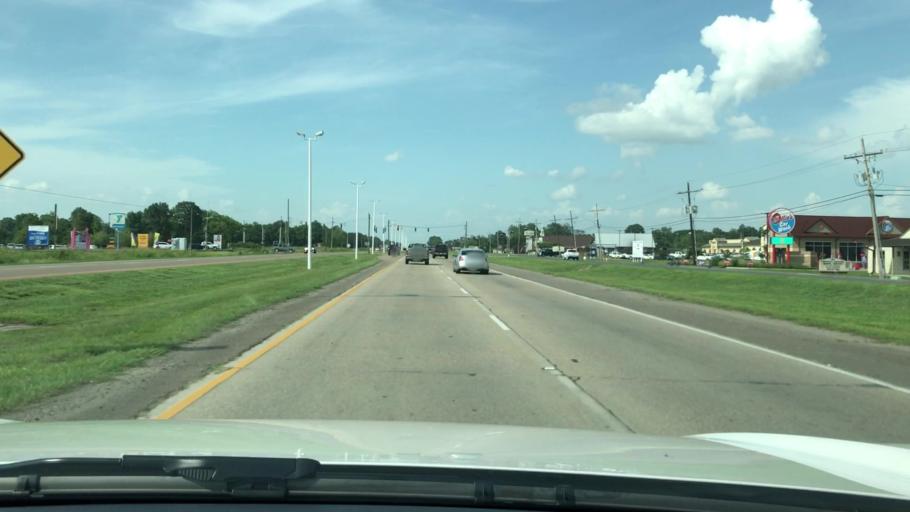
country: US
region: Louisiana
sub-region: West Baton Rouge Parish
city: Addis
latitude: 30.3723
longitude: -91.2553
